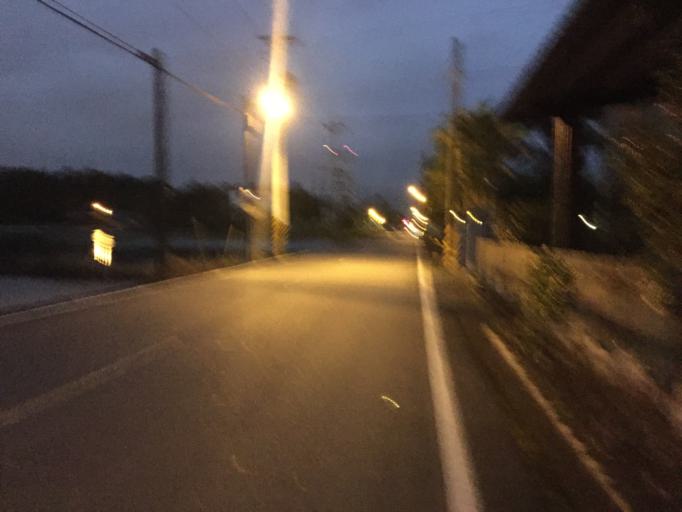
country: TW
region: Taiwan
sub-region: Yilan
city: Yilan
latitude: 24.6574
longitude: 121.7853
